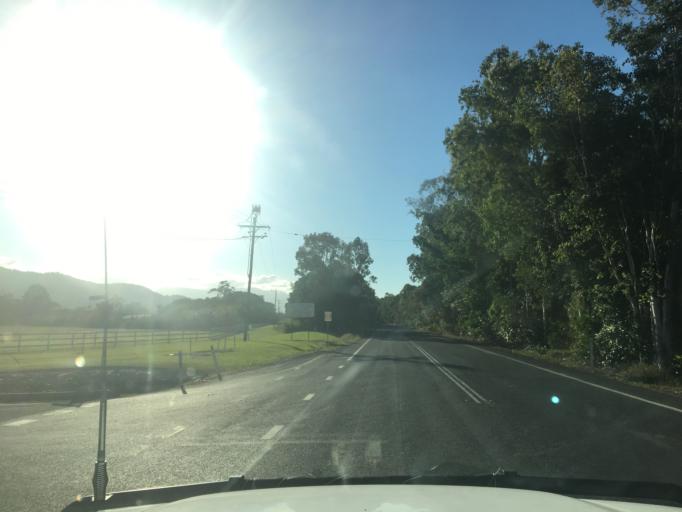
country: AU
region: Queensland
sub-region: Cairns
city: Port Douglas
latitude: -16.5267
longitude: 145.4602
